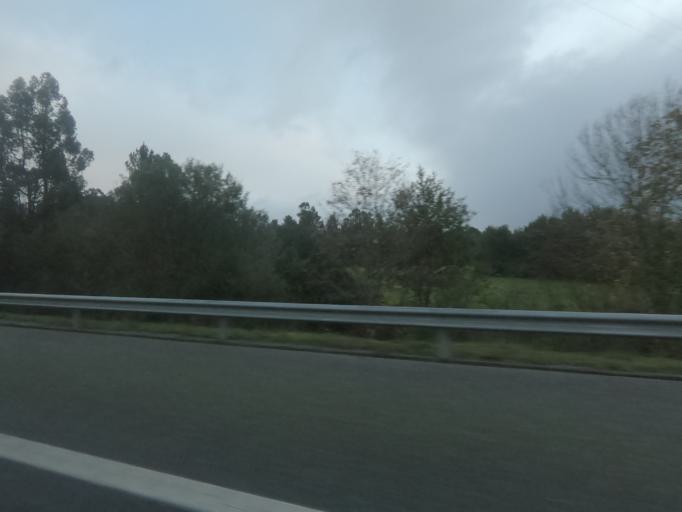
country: PT
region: Braga
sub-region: Barcelos
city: Galegos
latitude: 41.6224
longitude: -8.5559
